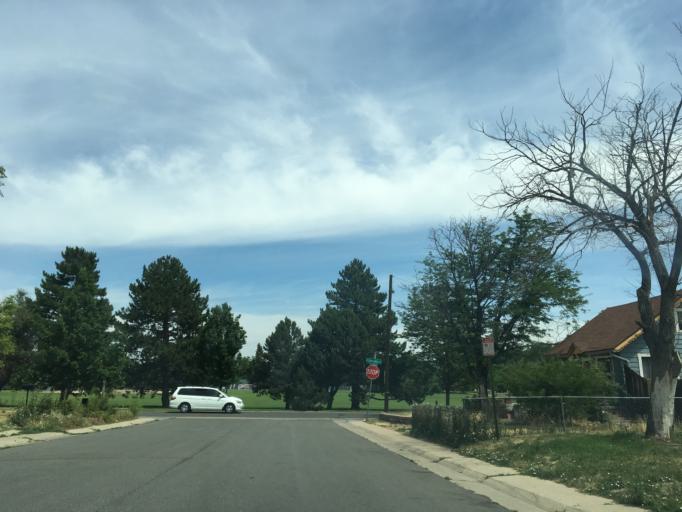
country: US
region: Colorado
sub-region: Arapahoe County
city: Sheridan
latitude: 39.6927
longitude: -105.0354
